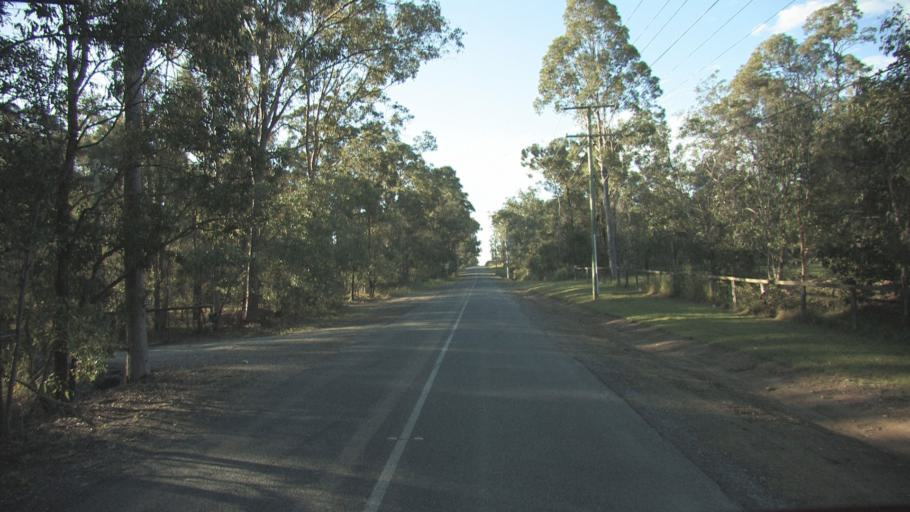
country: AU
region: Queensland
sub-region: Logan
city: Waterford West
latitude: -27.7282
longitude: 153.1468
